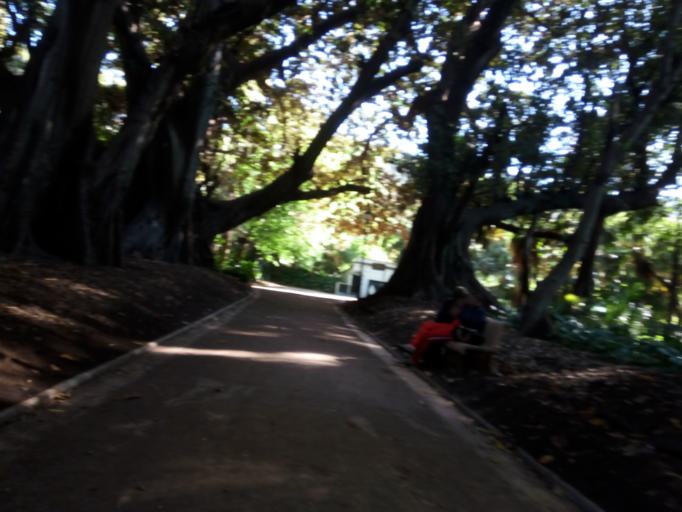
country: DZ
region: Alger
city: Algiers
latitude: 36.7461
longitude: 3.0759
